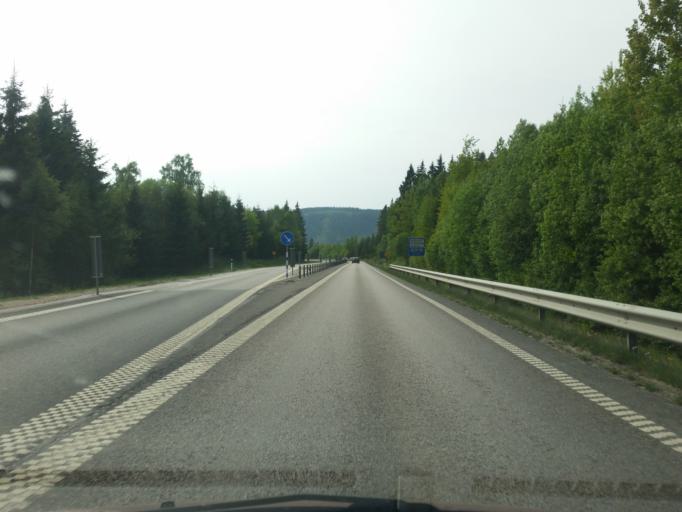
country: SE
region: Vaestra Goetaland
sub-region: Ulricehamns Kommun
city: Ulricehamn
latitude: 57.8090
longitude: 13.4483
